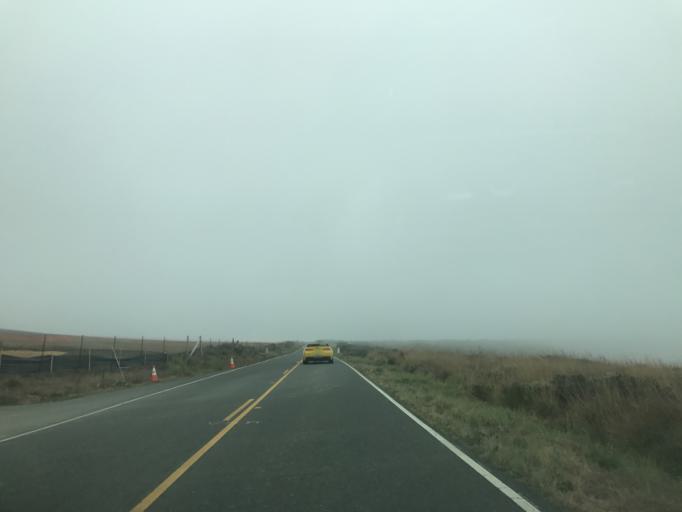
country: US
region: California
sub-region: Sonoma County
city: Monte Rio
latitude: 38.4597
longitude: -123.1432
